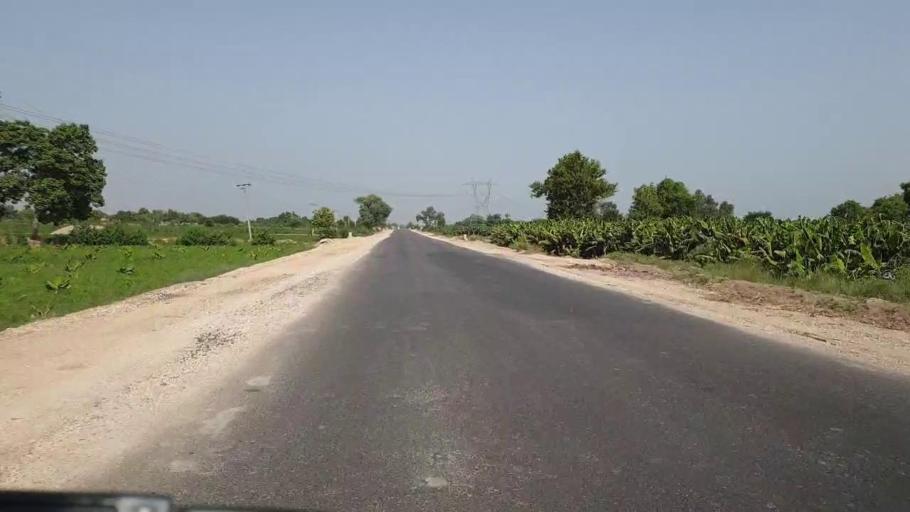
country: PK
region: Sindh
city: Sakrand
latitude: 26.2545
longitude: 68.1993
